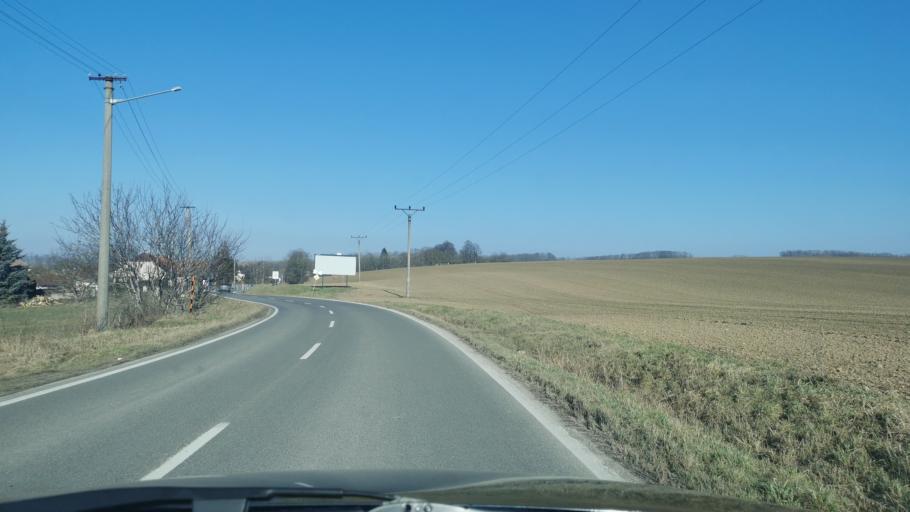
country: SK
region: Trnavsky
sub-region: Okres Senica
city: Senica
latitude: 48.6854
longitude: 17.3963
